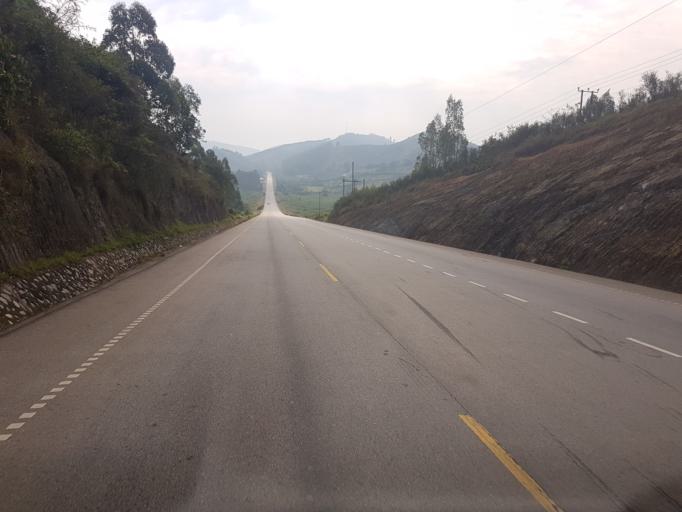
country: UG
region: Western Region
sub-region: Ntungamo District
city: Ntungamo
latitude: -0.7729
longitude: 30.2929
